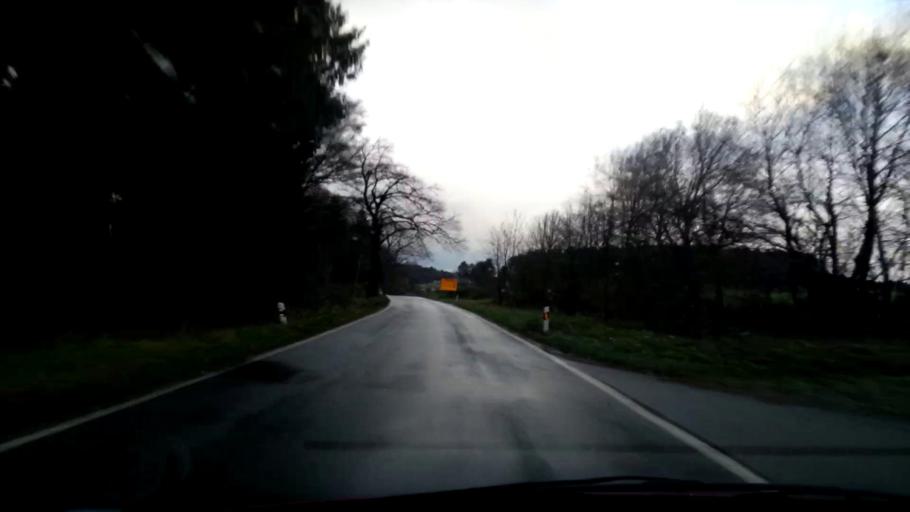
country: DE
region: Bavaria
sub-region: Upper Franconia
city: Aufsess
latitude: 49.9257
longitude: 11.1964
